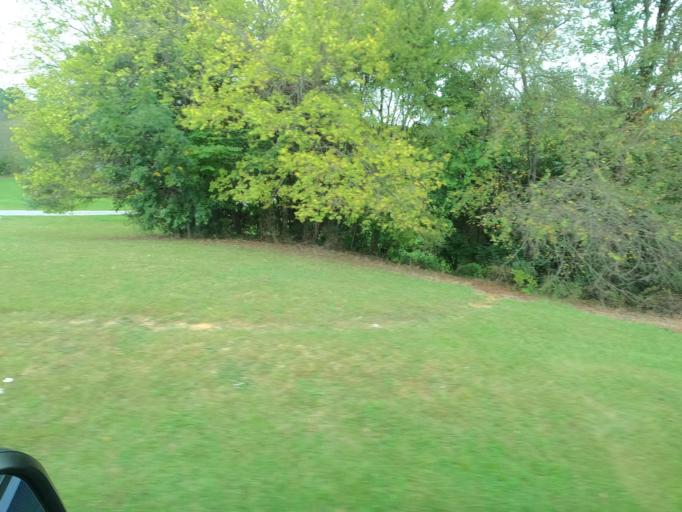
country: US
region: Tennessee
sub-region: Washington County
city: Jonesborough
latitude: 36.2552
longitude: -82.5414
